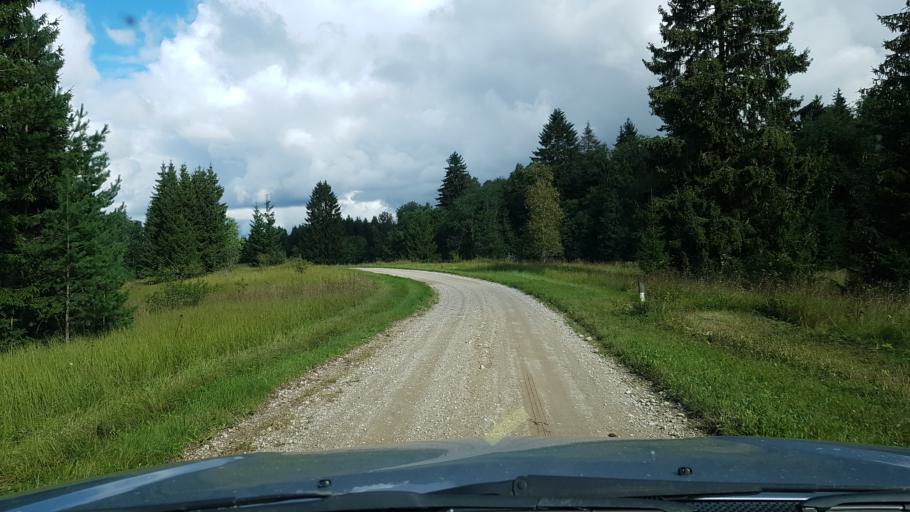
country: EE
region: Harju
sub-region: Raasiku vald
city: Arukula
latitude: 59.3068
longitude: 25.0785
